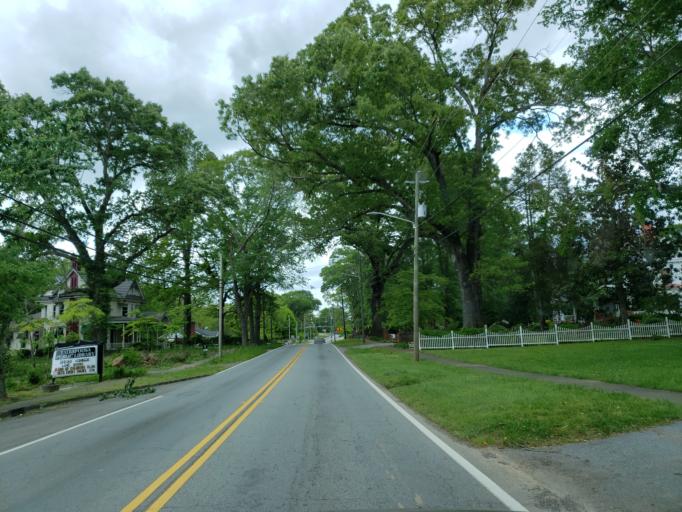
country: US
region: Georgia
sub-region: Haralson County
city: Tallapoosa
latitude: 33.7521
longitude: -85.2921
